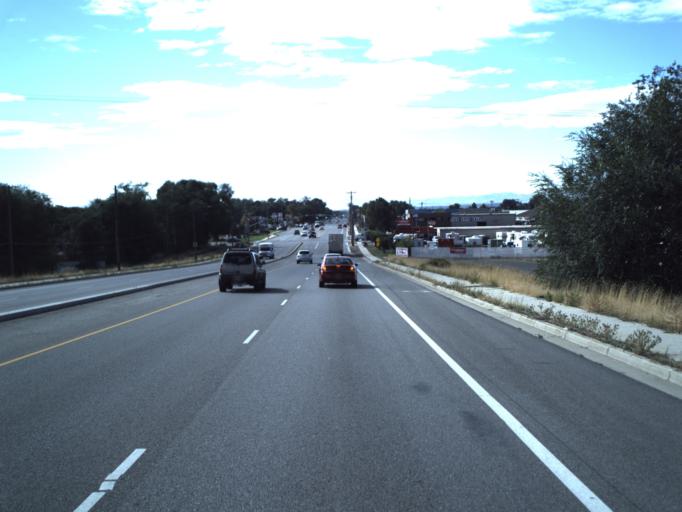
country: US
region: Utah
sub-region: Salt Lake County
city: Salt Lake City
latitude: 40.7630
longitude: -111.9392
